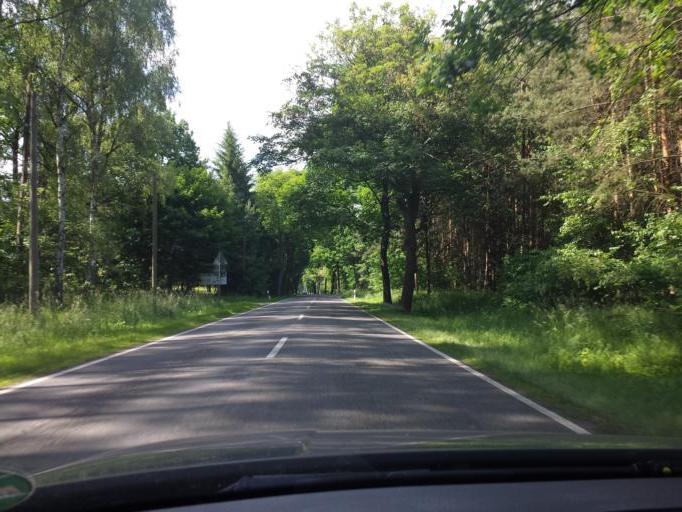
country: DE
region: Brandenburg
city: Ruthnick
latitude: 52.8741
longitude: 13.0068
